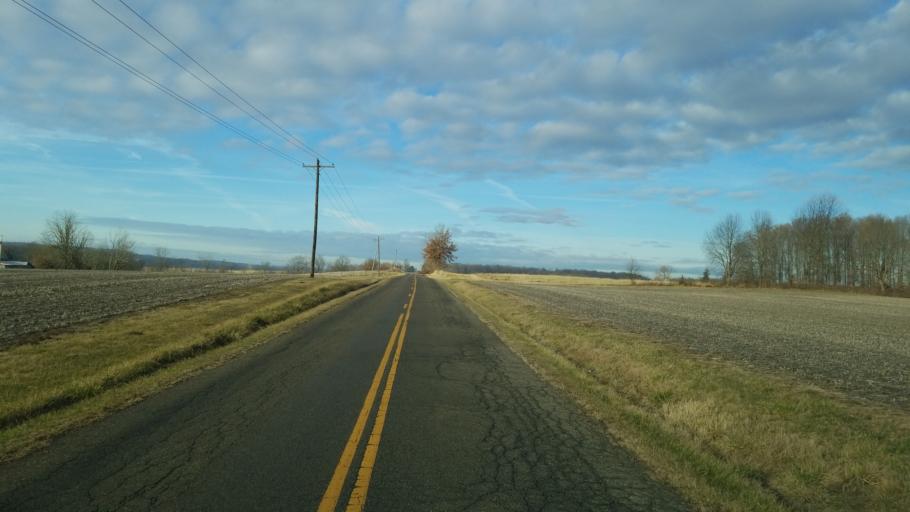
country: US
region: Ohio
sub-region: Knox County
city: Gambier
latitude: 40.3138
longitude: -82.3390
